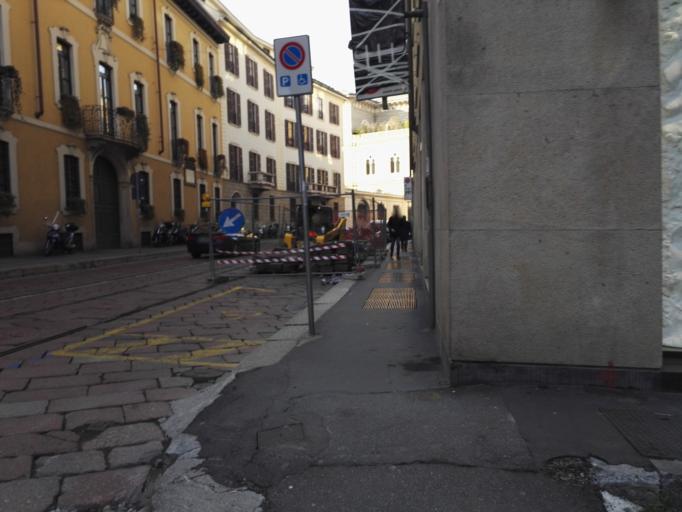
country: IT
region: Lombardy
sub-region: Citta metropolitana di Milano
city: Milano
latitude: 45.4700
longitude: 9.1912
